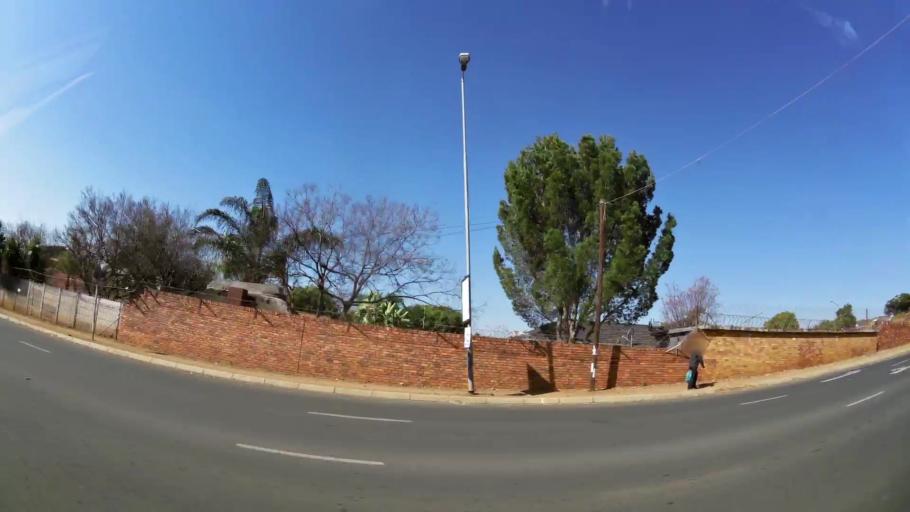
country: ZA
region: Gauteng
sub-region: City of Tshwane Metropolitan Municipality
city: Pretoria
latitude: -25.6785
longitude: 28.2540
